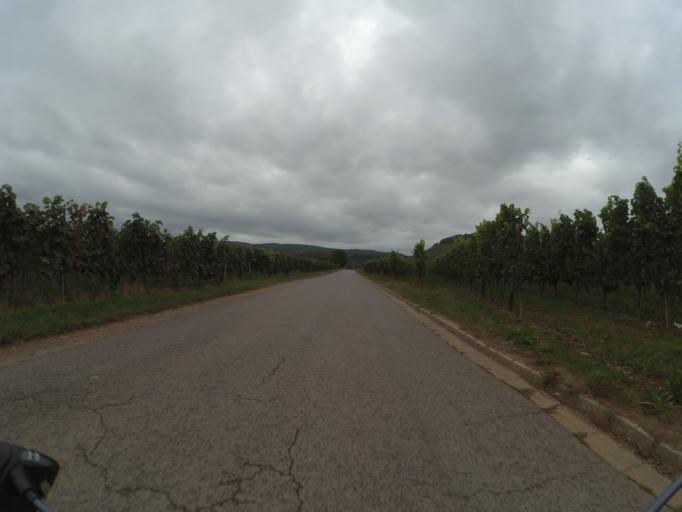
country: DE
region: Rheinland-Pfalz
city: Klusserath
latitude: 49.8319
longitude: 6.8523
